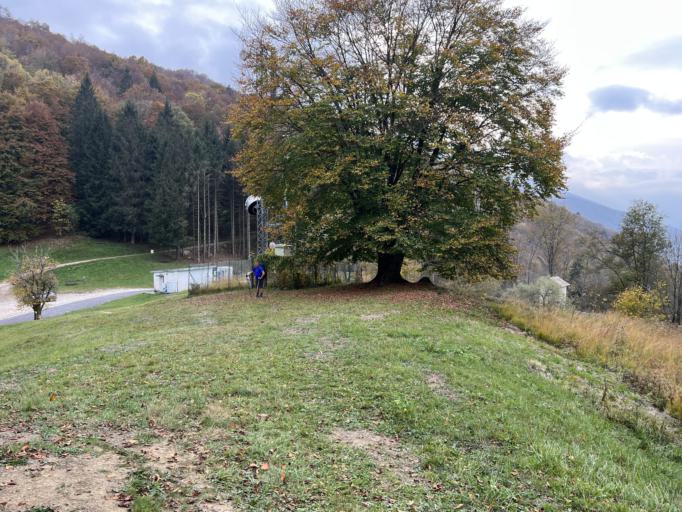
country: IT
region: Friuli Venezia Giulia
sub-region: Provincia di Pordenone
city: Andreis
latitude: 46.1965
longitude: 12.6590
